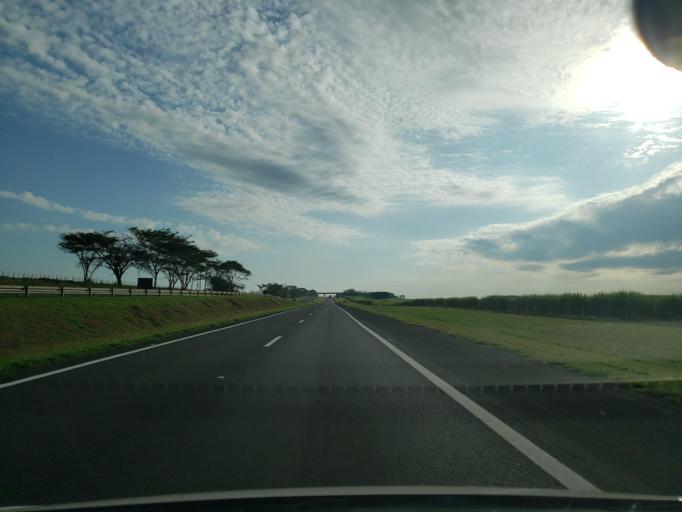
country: BR
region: Sao Paulo
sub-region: Valparaiso
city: Valparaiso
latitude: -21.2055
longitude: -50.7840
